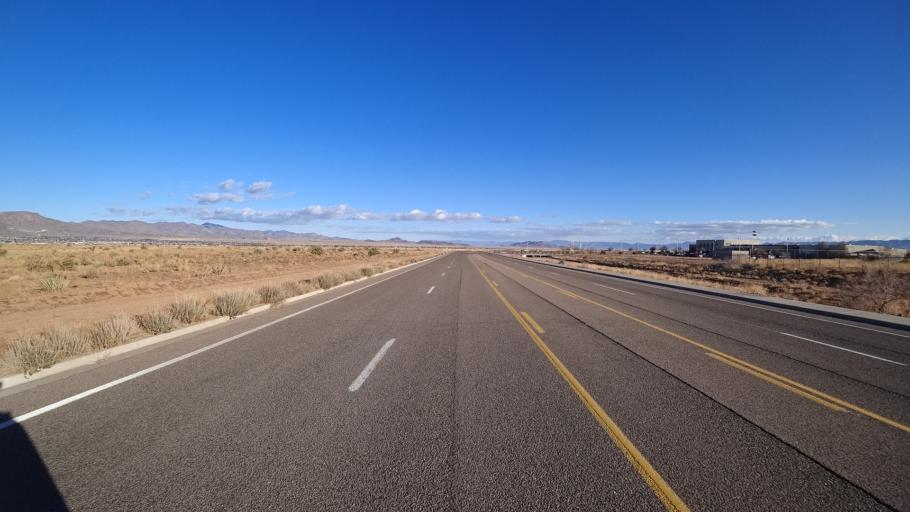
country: US
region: Arizona
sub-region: Mohave County
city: New Kingman-Butler
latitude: 35.2278
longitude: -113.9761
